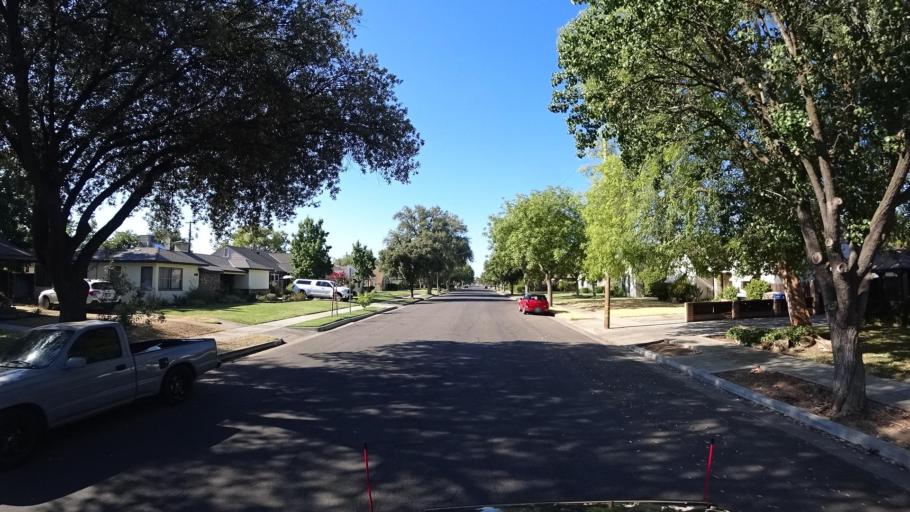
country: US
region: California
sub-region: Fresno County
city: Fresno
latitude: 36.7624
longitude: -119.8132
